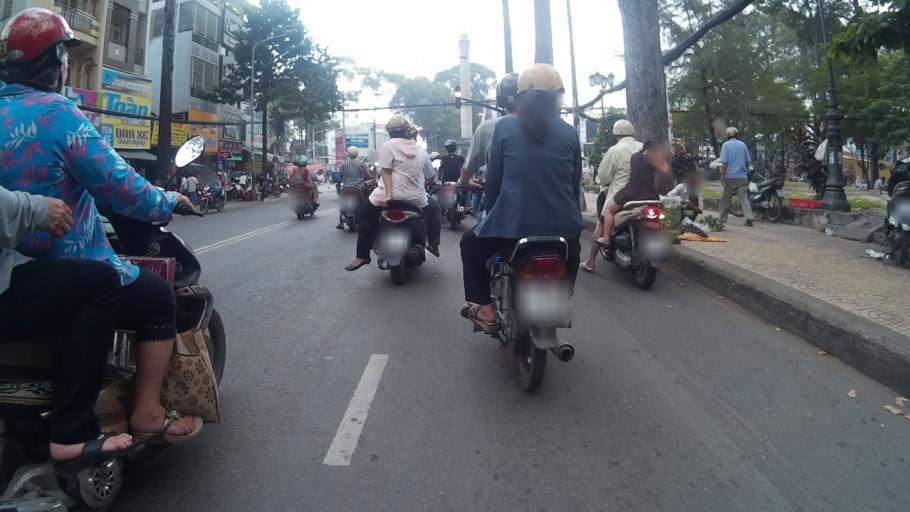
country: VN
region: Ho Chi Minh City
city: Quan Nam
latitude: 10.7598
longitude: 106.6679
